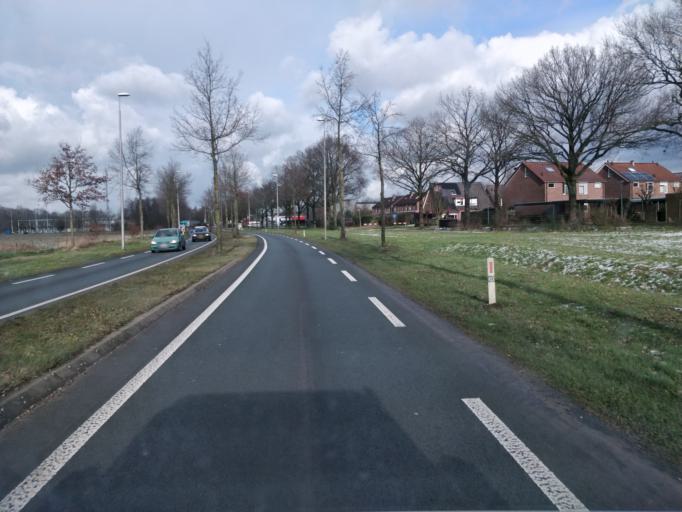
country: NL
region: Gelderland
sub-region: Gemeente Winterswijk
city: Winterswijk
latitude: 51.9703
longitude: 6.7016
